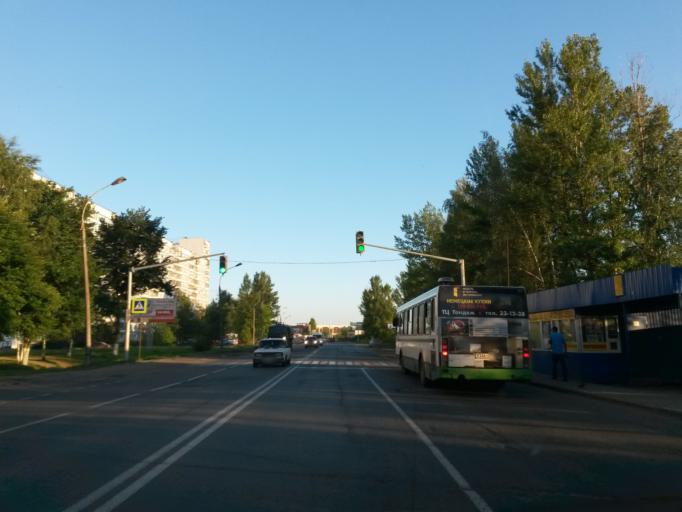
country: RU
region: Jaroslavl
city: Yaroslavl
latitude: 57.7053
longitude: 39.7591
